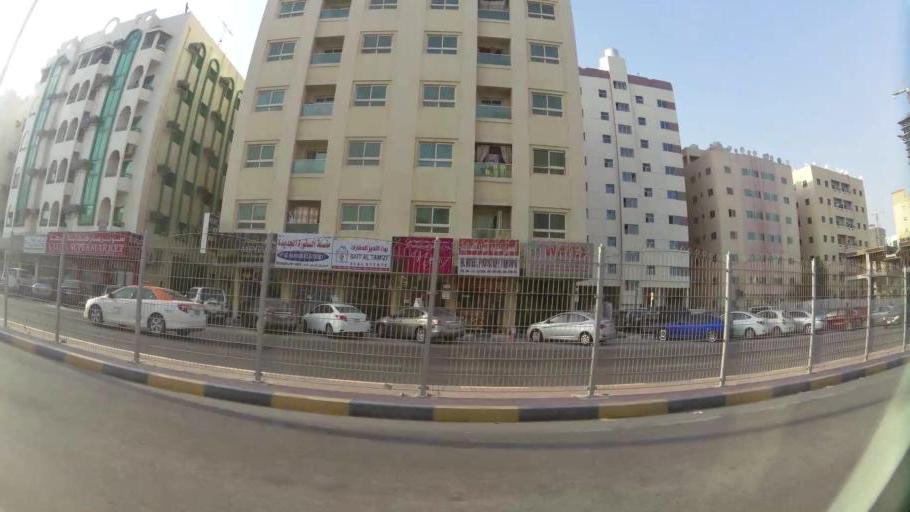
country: AE
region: Ajman
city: Ajman
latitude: 25.3868
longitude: 55.4517
